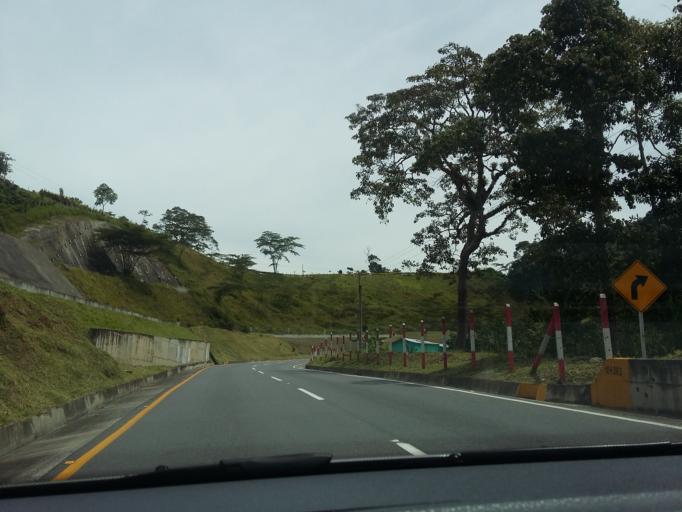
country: CO
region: Santander
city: Bucaramanga
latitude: 7.1165
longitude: -73.0789
